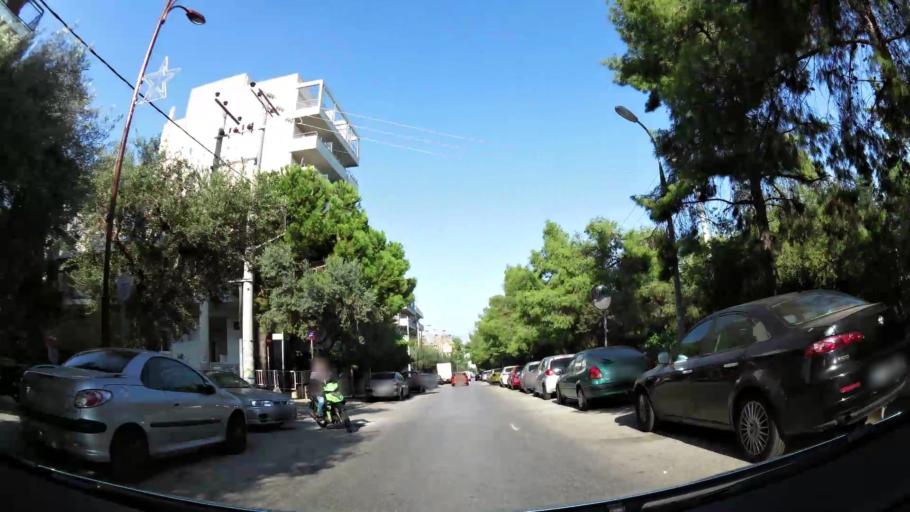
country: GR
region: Attica
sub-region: Nomos Attikis
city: Zografos
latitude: 37.9745
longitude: 23.7797
